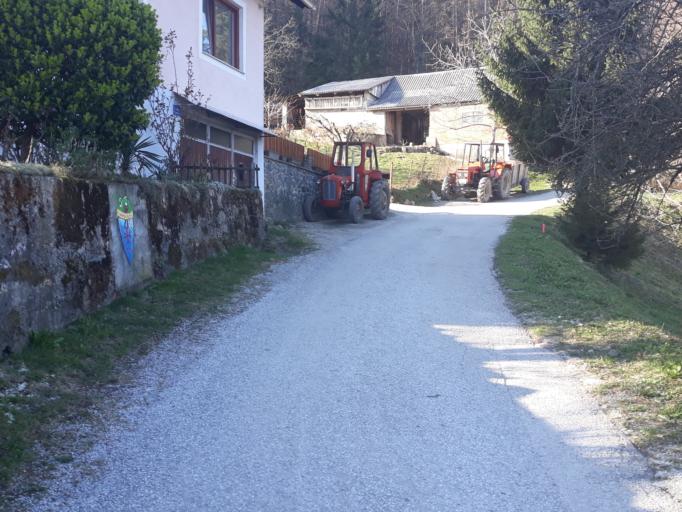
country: HR
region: Varazdinska
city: Ivanec
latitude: 46.1962
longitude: 16.1374
